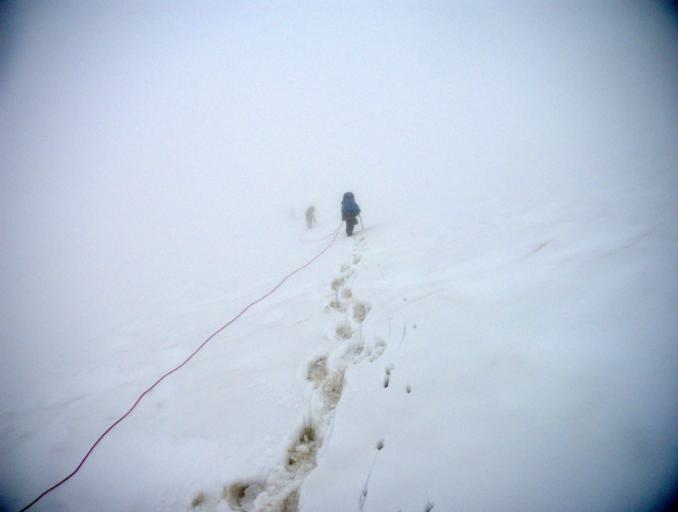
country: RU
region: Kabardino-Balkariya
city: Terskol
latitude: 43.3708
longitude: 42.4835
